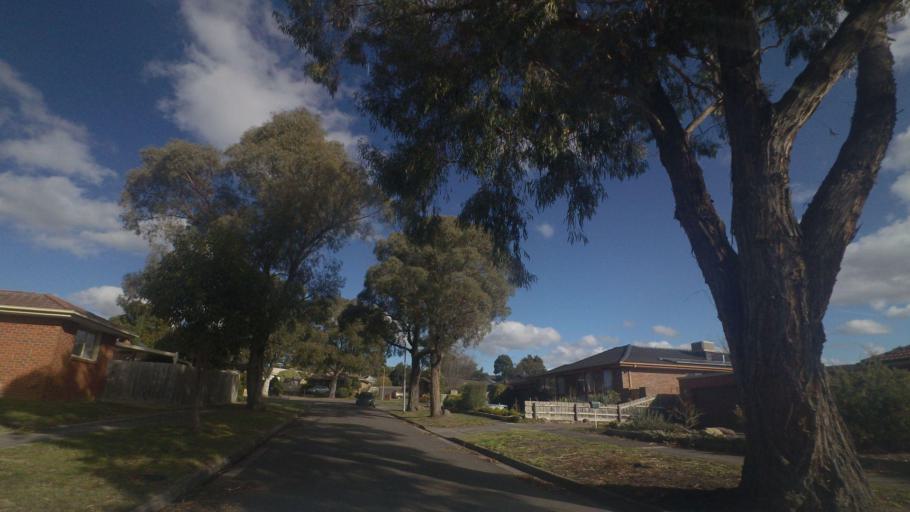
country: AU
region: Victoria
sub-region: Yarra Ranges
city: Lysterfield
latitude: -37.9163
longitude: 145.2736
